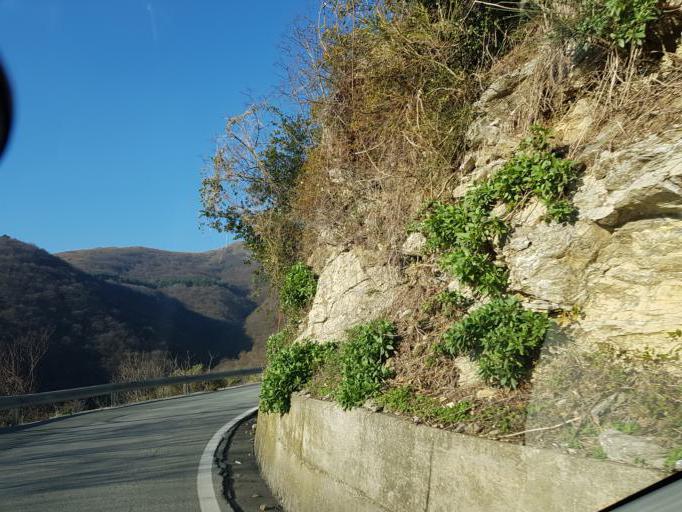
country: IT
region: Liguria
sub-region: Provincia di Genova
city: Piccarello
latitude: 44.4581
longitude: 8.9541
